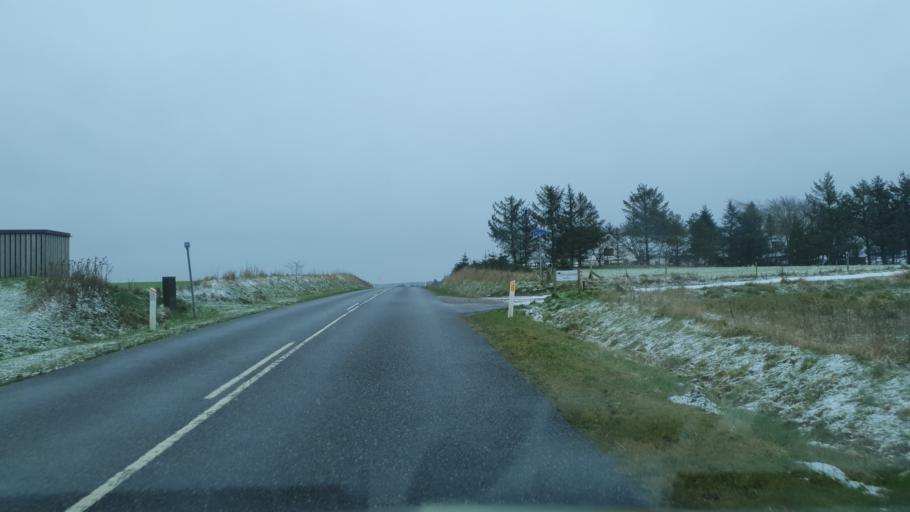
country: DK
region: North Denmark
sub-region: Jammerbugt Kommune
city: Brovst
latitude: 57.1262
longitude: 9.4807
